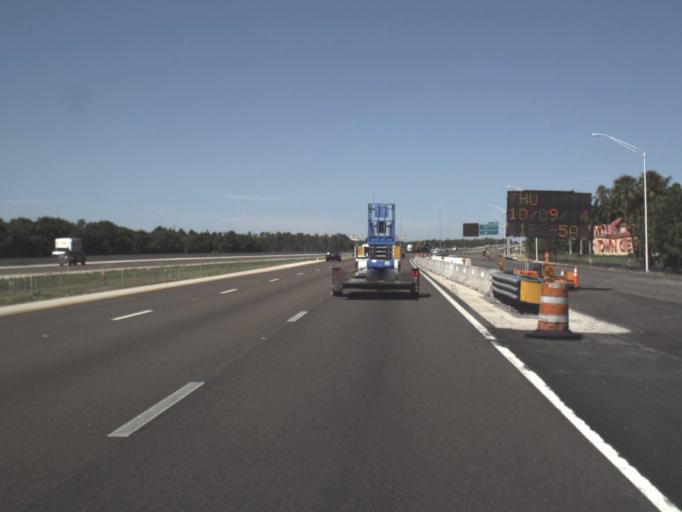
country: US
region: Florida
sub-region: Lee County
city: Three Oaks
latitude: 26.4820
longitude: -81.7933
